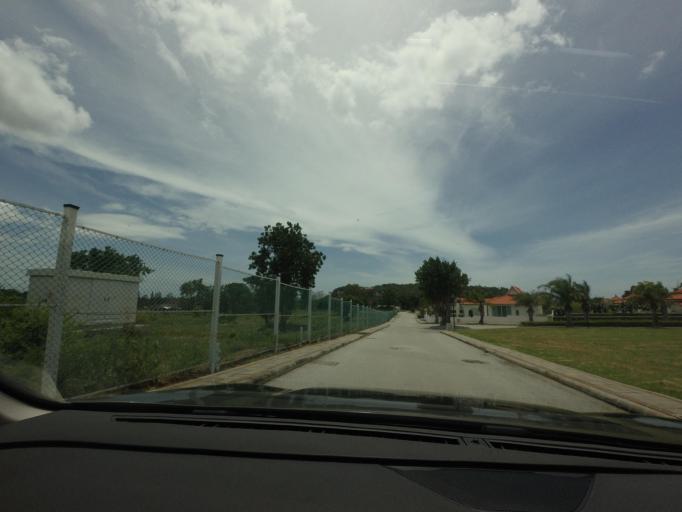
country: TH
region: Prachuap Khiri Khan
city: Hua Hin
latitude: 12.5165
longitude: 99.9594
